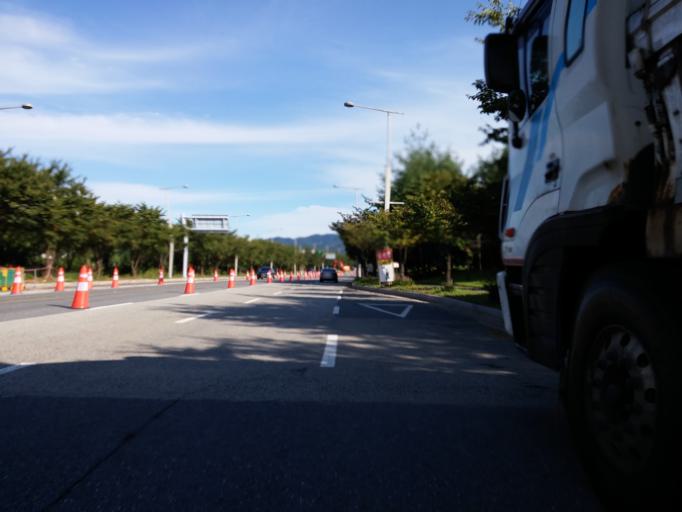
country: KR
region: Daejeon
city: Songgang-dong
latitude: 36.4349
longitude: 127.3936
